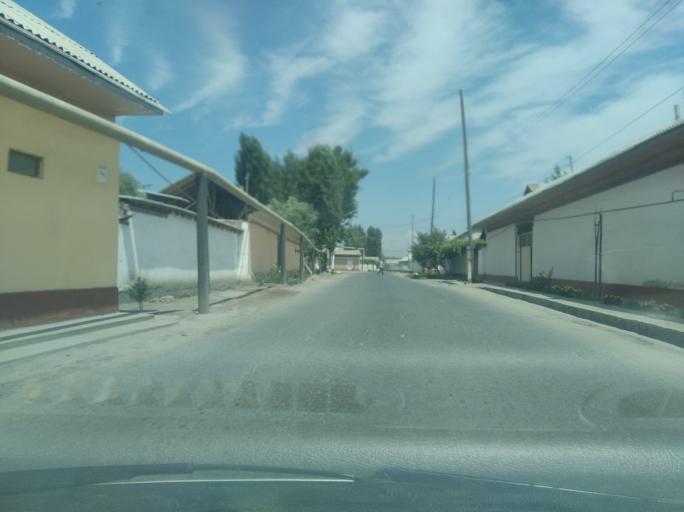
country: UZ
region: Andijon
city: Khujaobod
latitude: 40.6325
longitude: 72.4492
